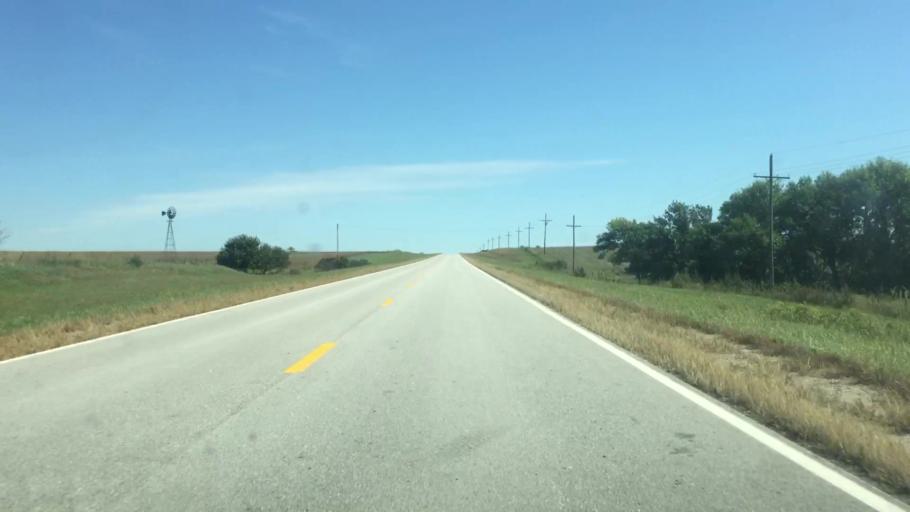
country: US
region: Nebraska
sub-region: Gage County
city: Wymore
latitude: 40.0453
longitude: -96.7406
